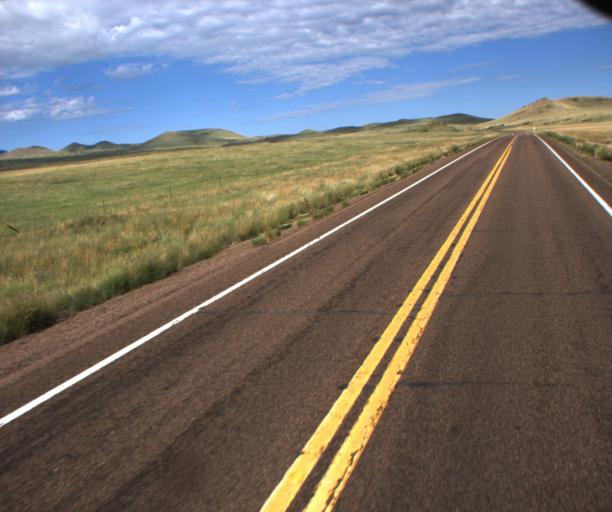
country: US
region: Arizona
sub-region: Apache County
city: Springerville
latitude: 34.2002
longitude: -109.3970
